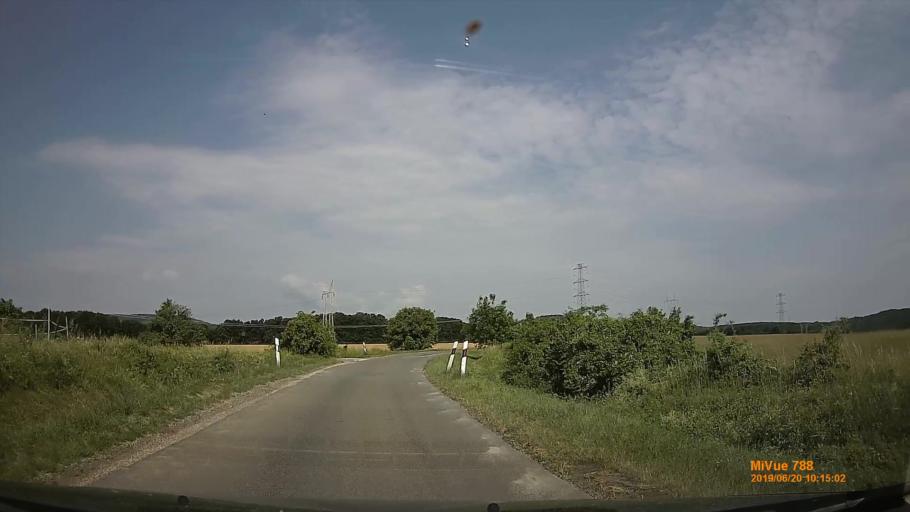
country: HU
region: Baranya
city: Mecseknadasd
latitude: 46.1888
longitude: 18.4671
